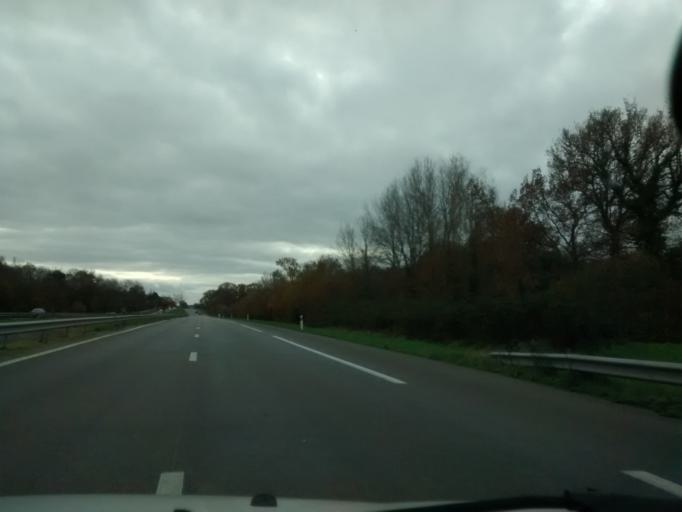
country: FR
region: Brittany
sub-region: Departement d'Ille-et-Vilaine
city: Miniac-Morvan
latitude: 48.4850
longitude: -1.9082
